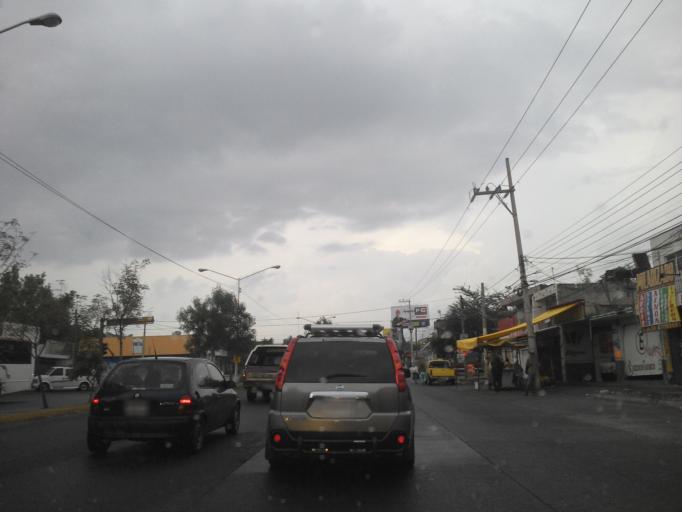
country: MX
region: Jalisco
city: Guadalajara
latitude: 20.6223
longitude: -103.3720
